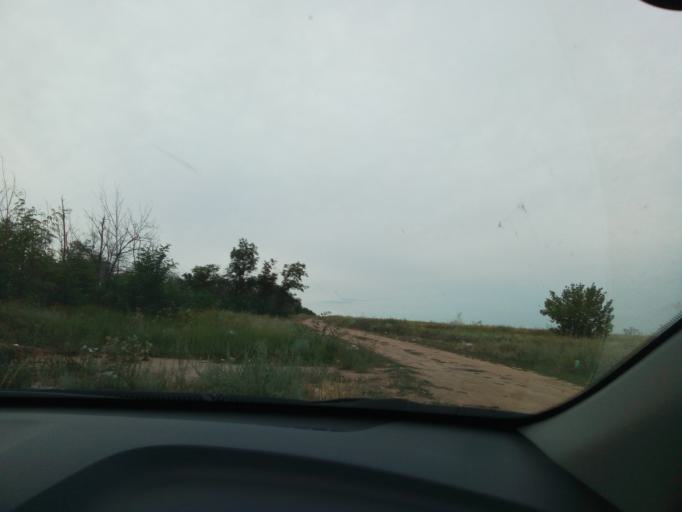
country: RU
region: Volgograd
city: Dubovka
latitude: 49.1403
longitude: 44.8278
